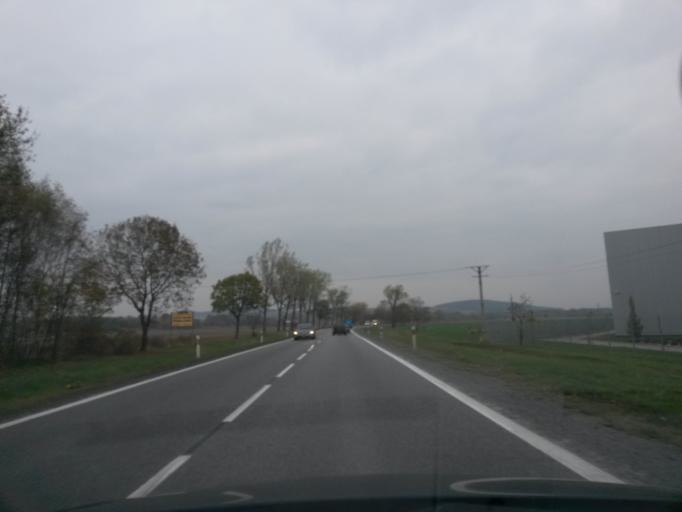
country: PL
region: Lower Silesian Voivodeship
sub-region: Powiat zabkowicki
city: Bardo
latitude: 50.5123
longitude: 16.7590
